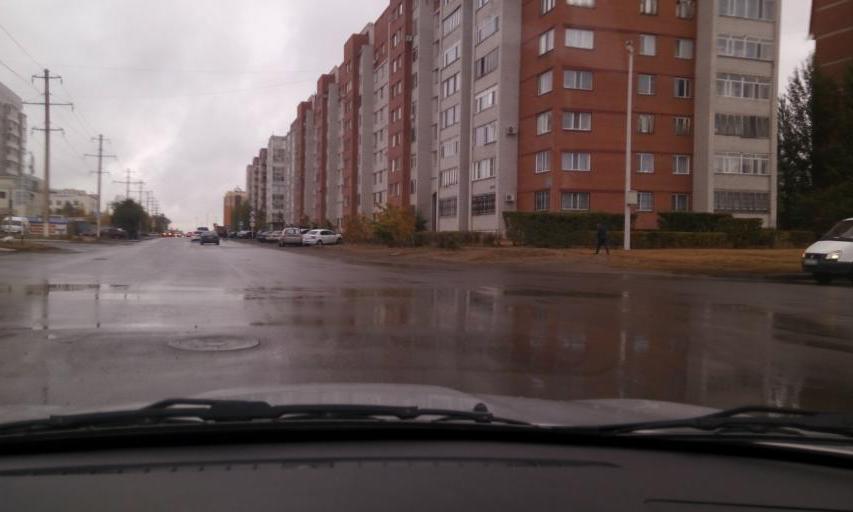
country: KZ
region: Astana Qalasy
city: Astana
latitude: 51.1649
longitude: 71.4000
